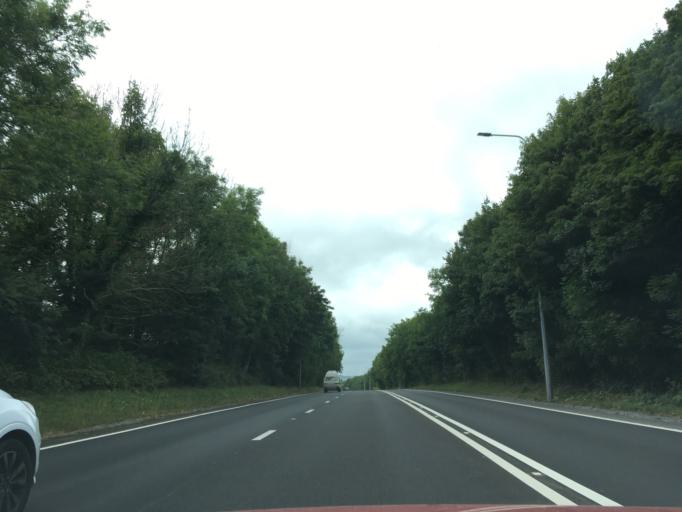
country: GB
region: Wales
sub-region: Carmarthenshire
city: Saint Clears
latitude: 51.8190
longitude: -4.5125
